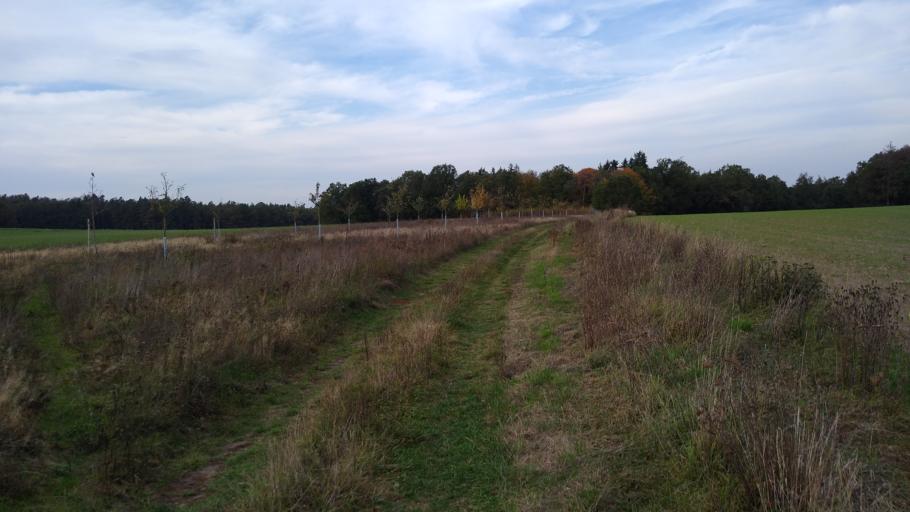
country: DE
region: Bavaria
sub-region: Regierungsbezirk Mittelfranken
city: Obermichelbach
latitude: 49.5010
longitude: 10.9256
